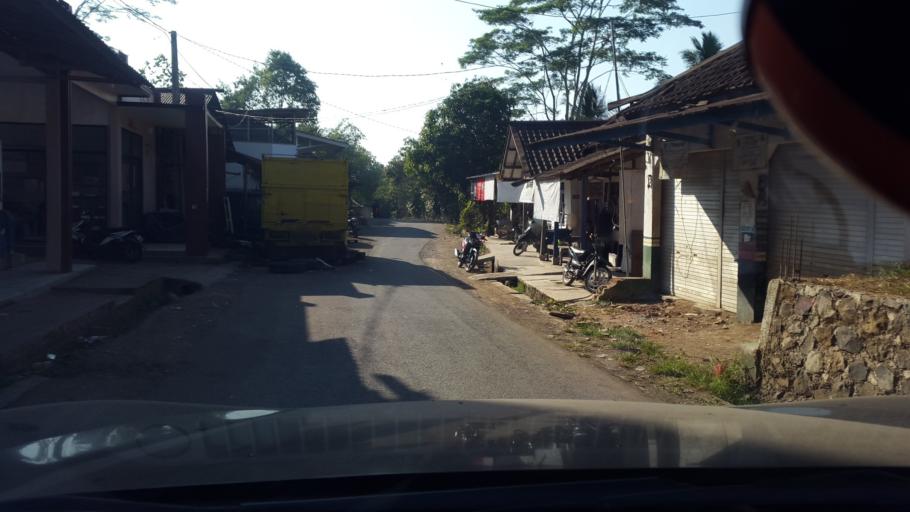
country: ID
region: West Java
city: Curugkembar Satu
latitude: -7.2166
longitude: 106.9393
